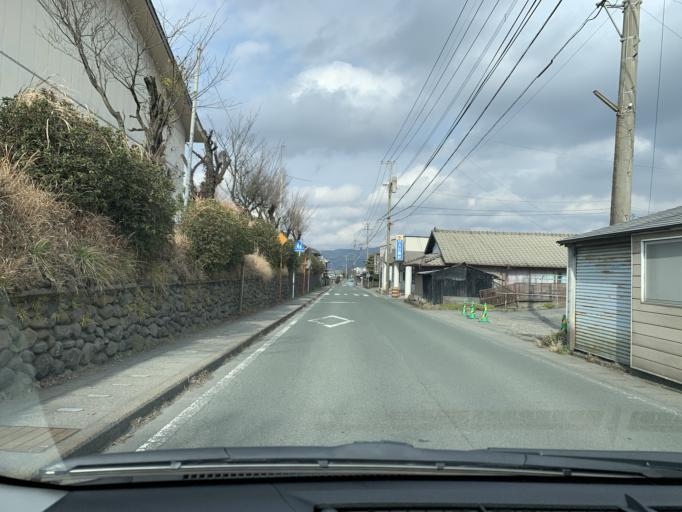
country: JP
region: Kumamoto
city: Aso
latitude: 32.9418
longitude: 131.1157
